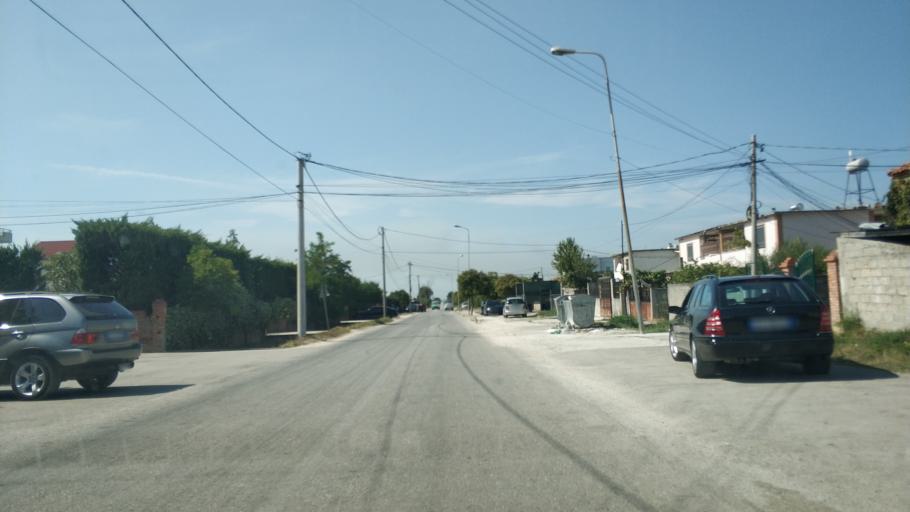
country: AL
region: Fier
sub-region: Rrethi i Fierit
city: Dermenas
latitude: 40.7456
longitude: 19.4924
